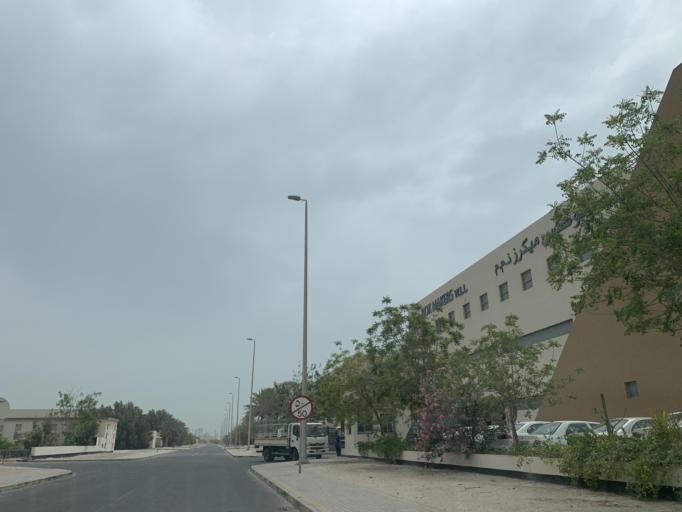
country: BH
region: Muharraq
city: Al Hadd
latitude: 26.2161
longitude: 50.6621
